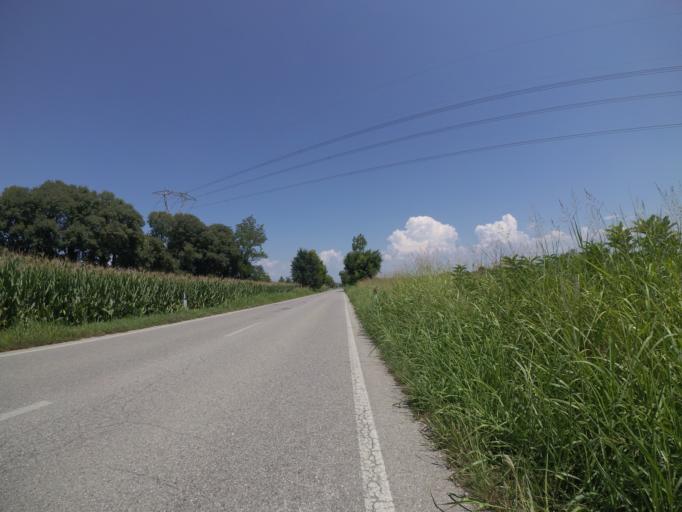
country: IT
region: Friuli Venezia Giulia
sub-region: Provincia di Udine
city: Mortegliano
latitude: 45.9329
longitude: 13.1591
